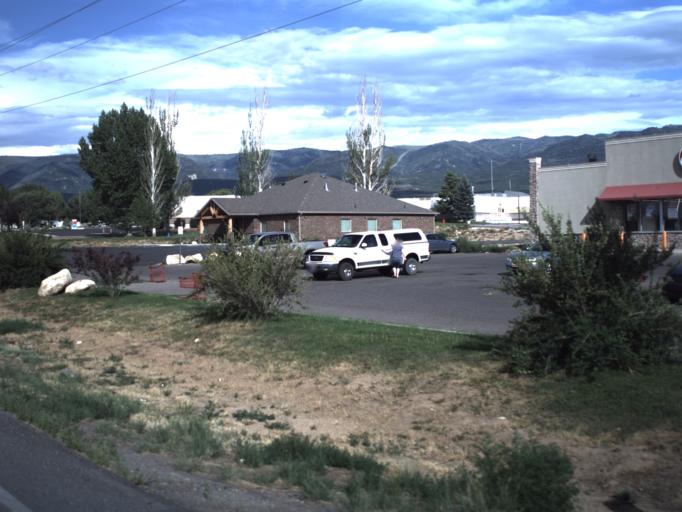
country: US
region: Utah
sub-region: Sanpete County
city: Mount Pleasant
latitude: 39.5315
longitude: -111.4632
